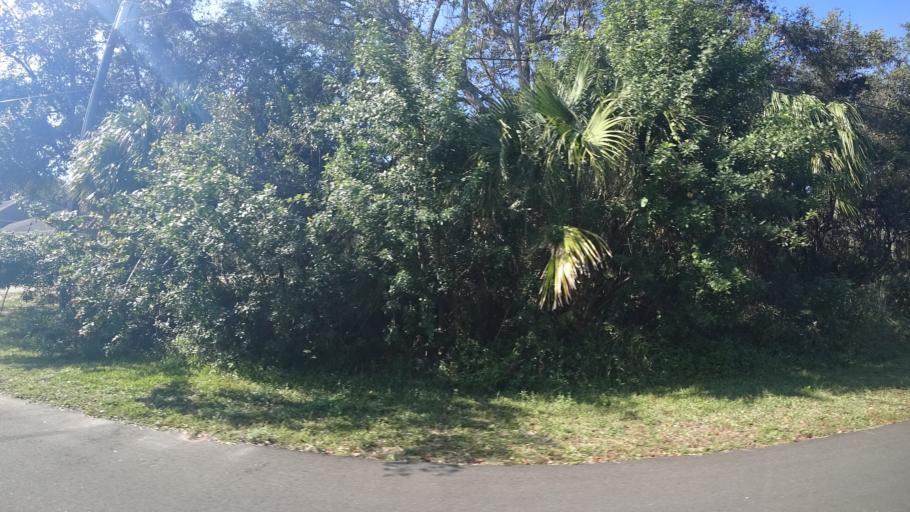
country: US
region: Florida
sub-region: Charlotte County
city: Port Charlotte
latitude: 27.0632
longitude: -82.1194
